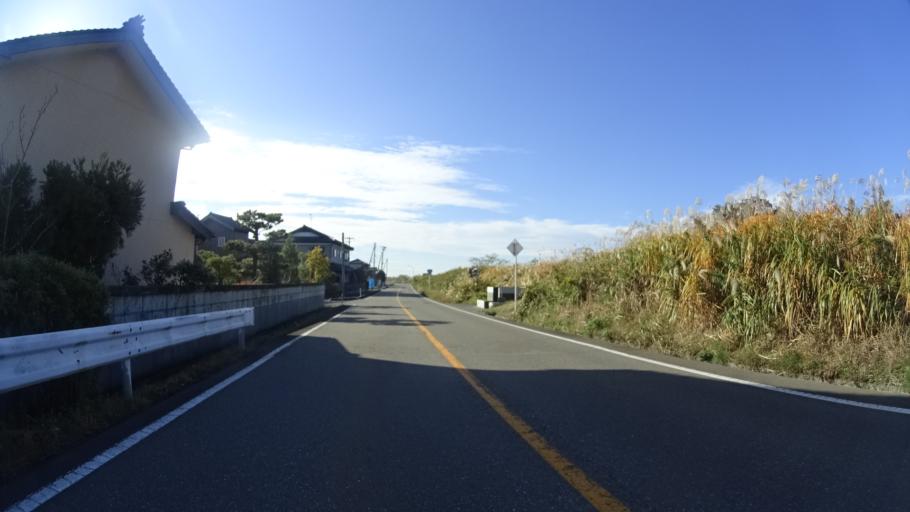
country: JP
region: Niigata
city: Yoshida-kasugacho
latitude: 37.5895
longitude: 138.8367
